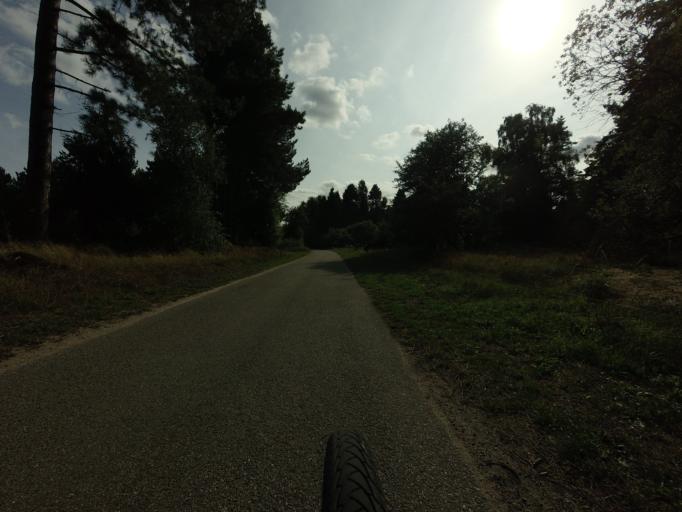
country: DK
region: Zealand
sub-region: Vordingborg Kommune
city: Praesto
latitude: 55.1648
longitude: 12.0938
